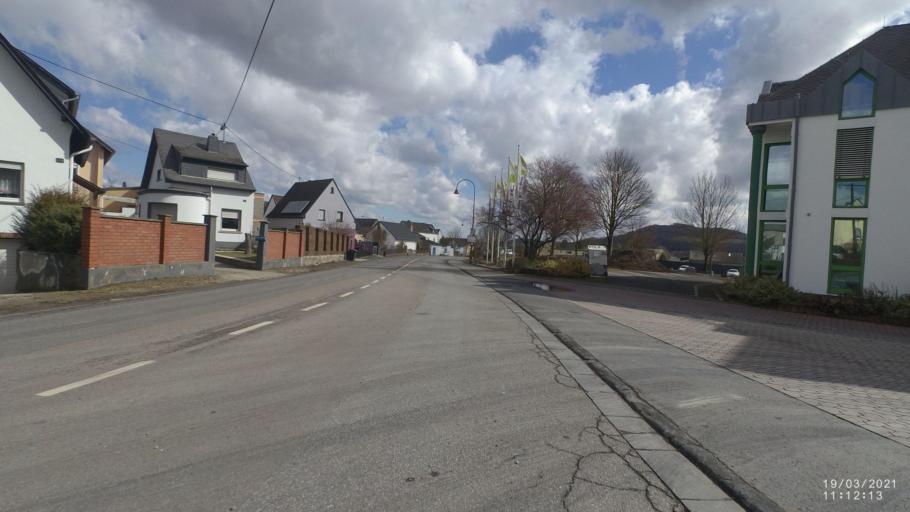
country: DE
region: Rheinland-Pfalz
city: Kruft
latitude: 50.3817
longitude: 7.3295
